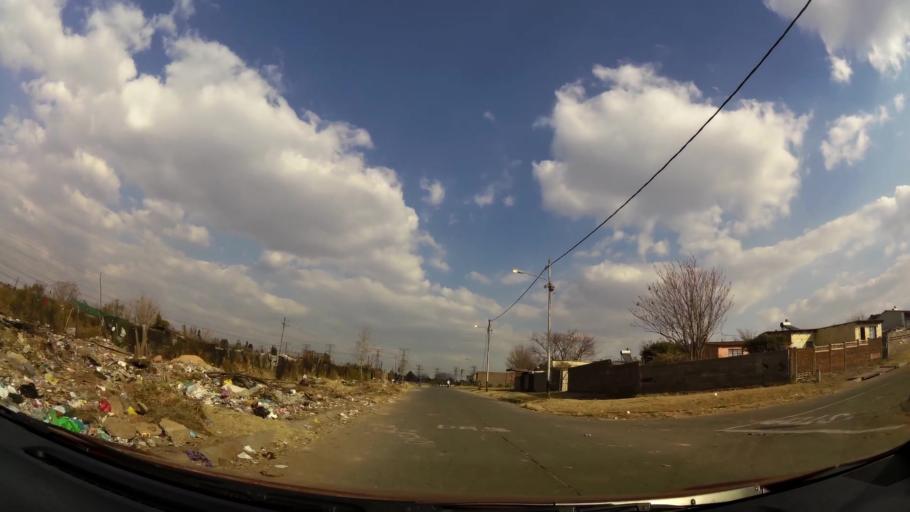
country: ZA
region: Gauteng
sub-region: City of Johannesburg Metropolitan Municipality
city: Soweto
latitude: -26.2304
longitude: 27.9427
